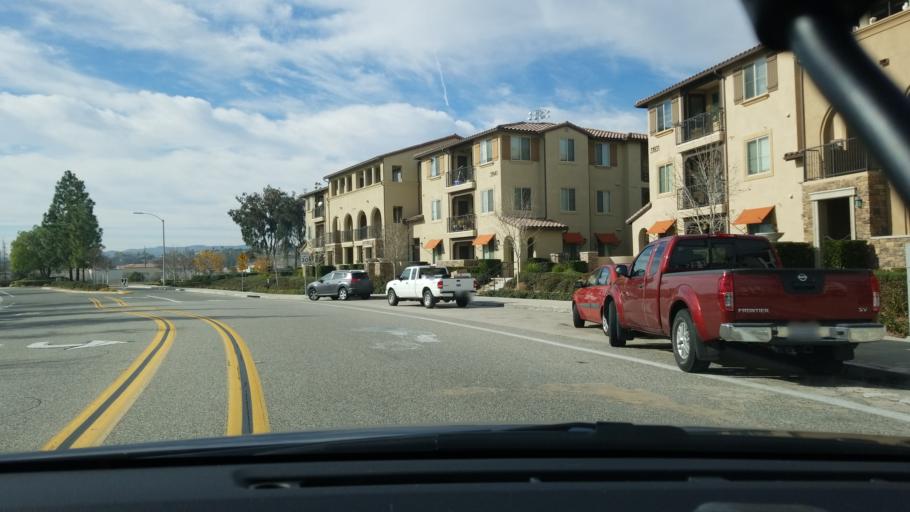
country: US
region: California
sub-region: Riverside County
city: Temecula
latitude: 33.4836
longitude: -117.0978
